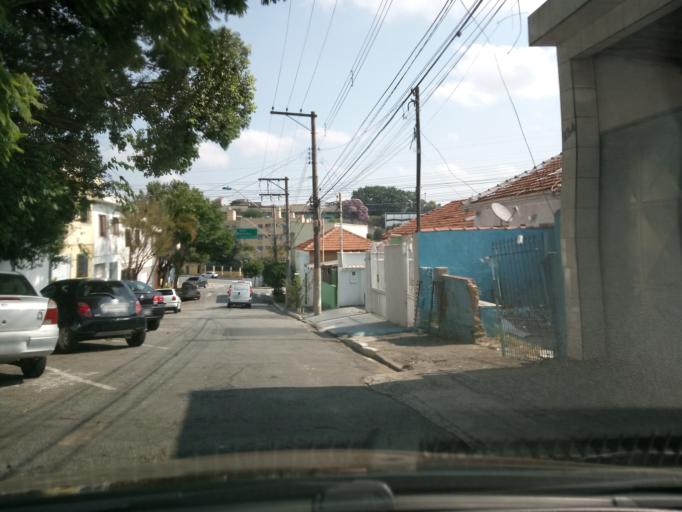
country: BR
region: Sao Paulo
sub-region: Sao Caetano Do Sul
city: Sao Caetano do Sul
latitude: -23.6331
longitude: -46.5756
